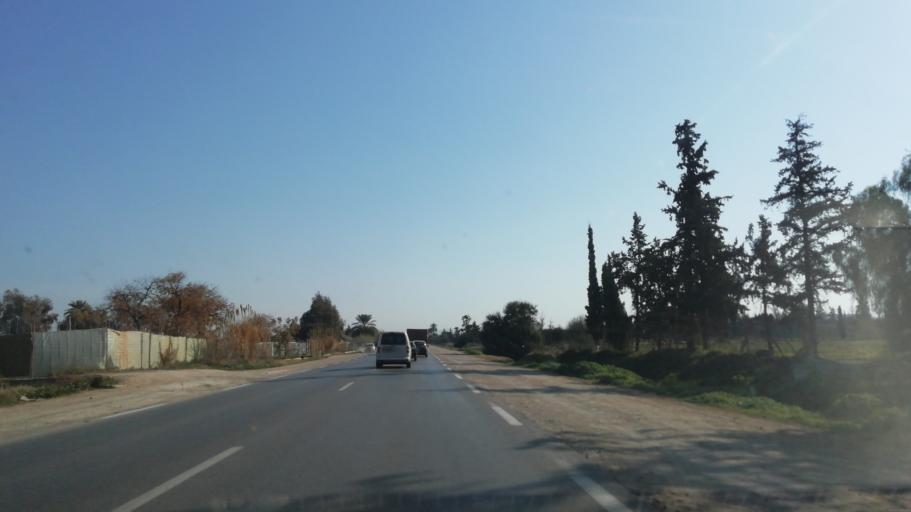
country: DZ
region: Relizane
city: Relizane
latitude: 35.7228
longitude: 0.4926
